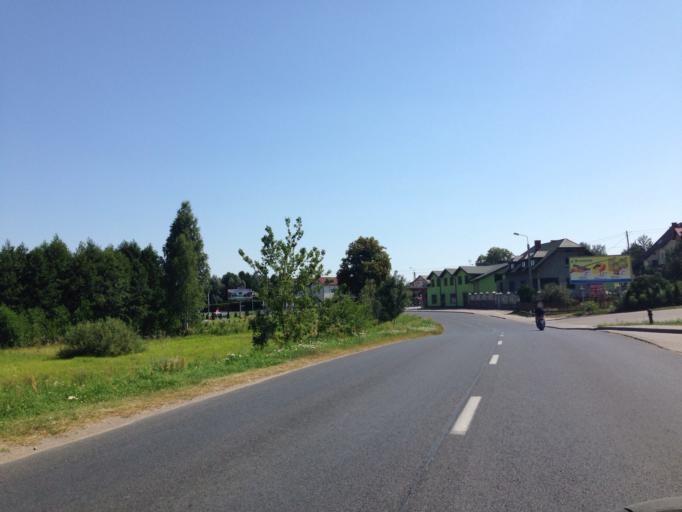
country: PL
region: Kujawsko-Pomorskie
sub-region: Powiat brodnicki
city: Bartniczka
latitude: 53.2499
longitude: 19.6053
